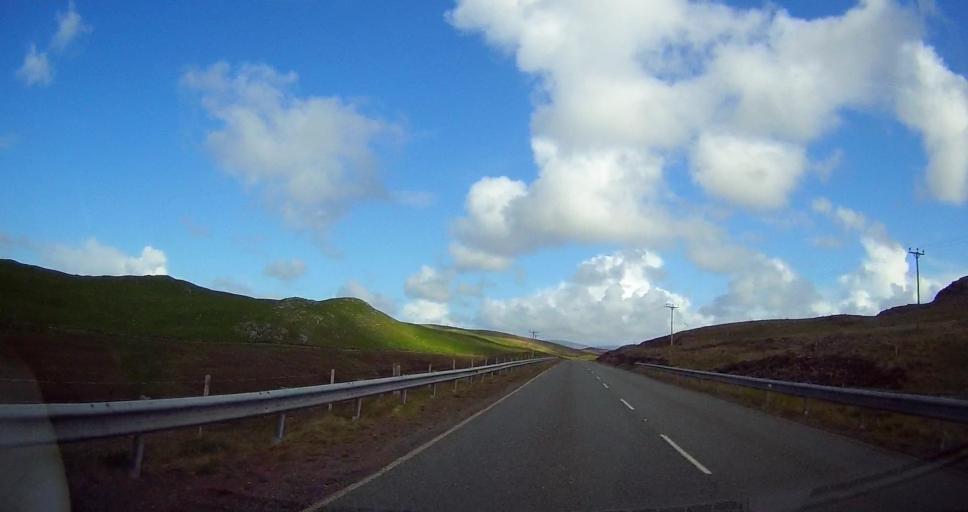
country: GB
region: Scotland
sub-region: Shetland Islands
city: Lerwick
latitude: 60.4214
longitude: -1.3944
